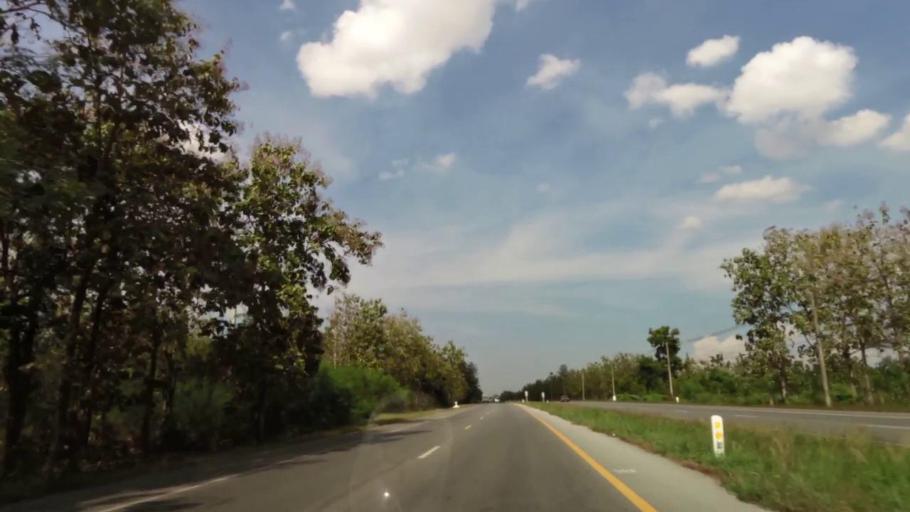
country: TH
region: Uttaradit
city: Thong Saen Khan
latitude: 17.5040
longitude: 100.2293
